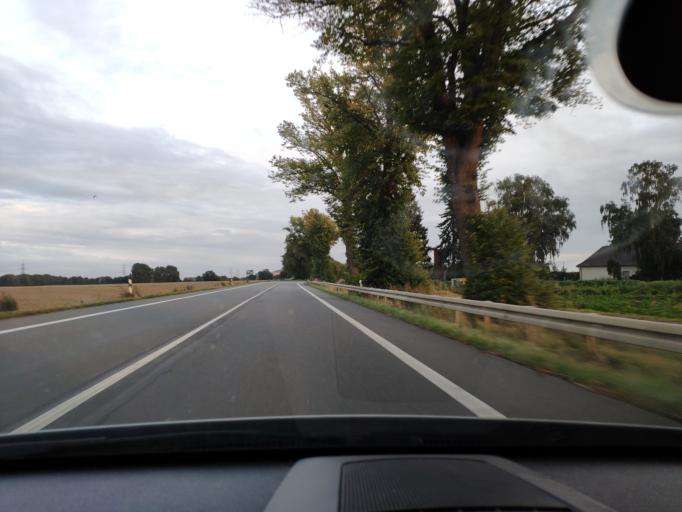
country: DE
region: North Rhine-Westphalia
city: Baesweiler
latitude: 50.9425
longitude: 6.1946
